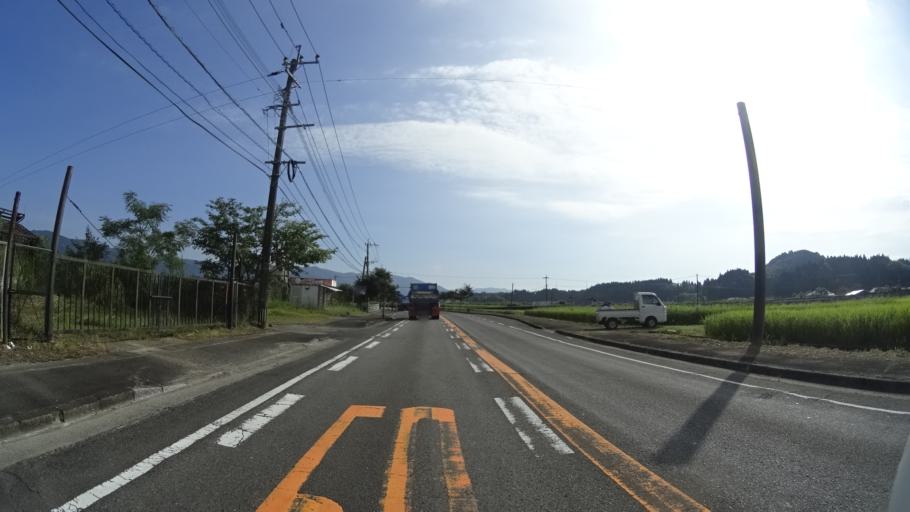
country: JP
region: Kagoshima
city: Okuchi-shinohara
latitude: 32.0411
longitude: 130.7610
